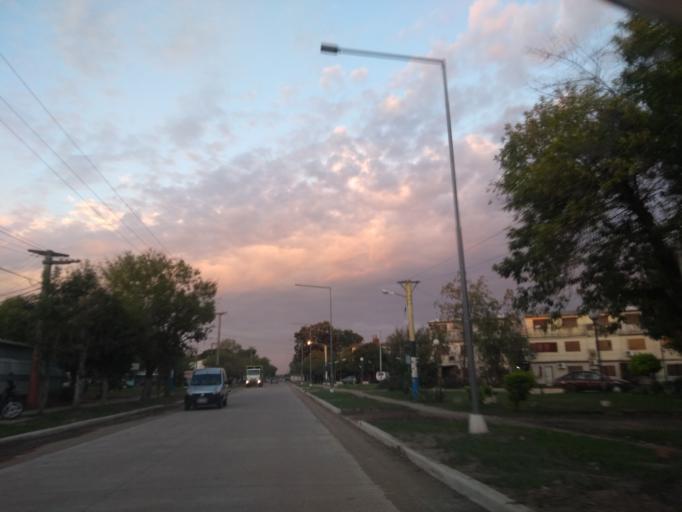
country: AR
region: Chaco
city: Resistencia
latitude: -27.4837
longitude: -58.9868
